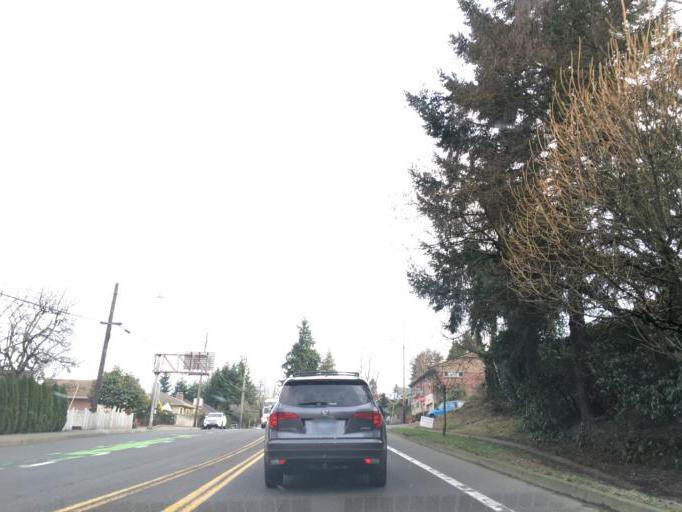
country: US
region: Oregon
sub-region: Clackamas County
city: Lake Oswego
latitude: 45.4684
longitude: -122.6861
